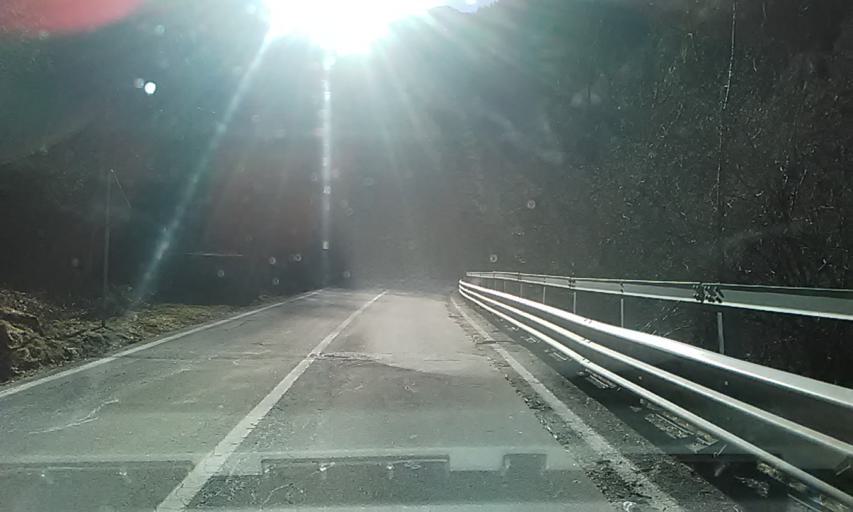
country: IT
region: Piedmont
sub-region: Provincia di Vercelli
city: Rimasco
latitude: 45.8491
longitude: 8.0670
